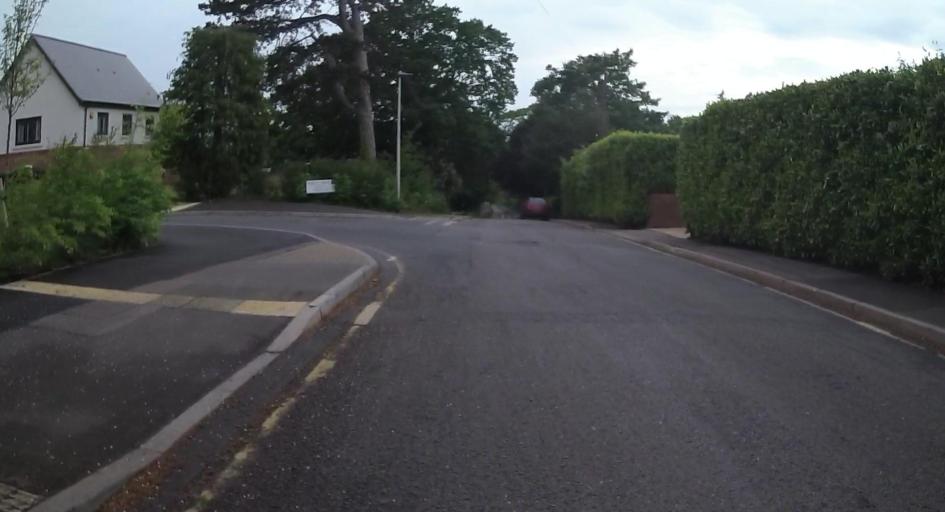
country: GB
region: England
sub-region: Bracknell Forest
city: Bracknell
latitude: 51.4216
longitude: -0.7463
